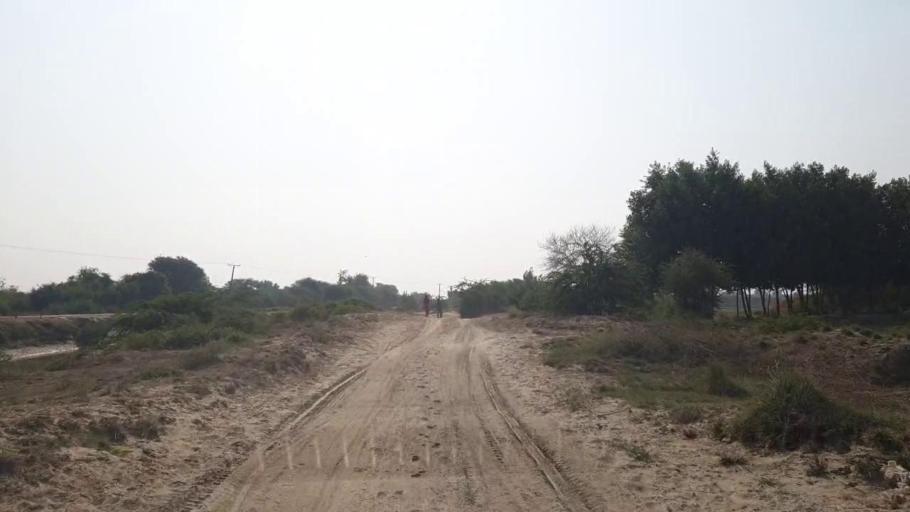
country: PK
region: Sindh
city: Matli
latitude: 24.9543
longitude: 68.6026
